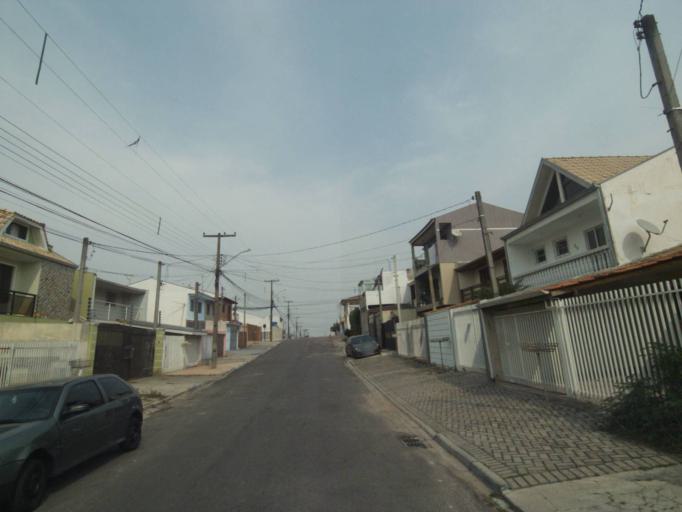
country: BR
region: Parana
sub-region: Sao Jose Dos Pinhais
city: Sao Jose dos Pinhais
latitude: -25.5266
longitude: -49.2742
